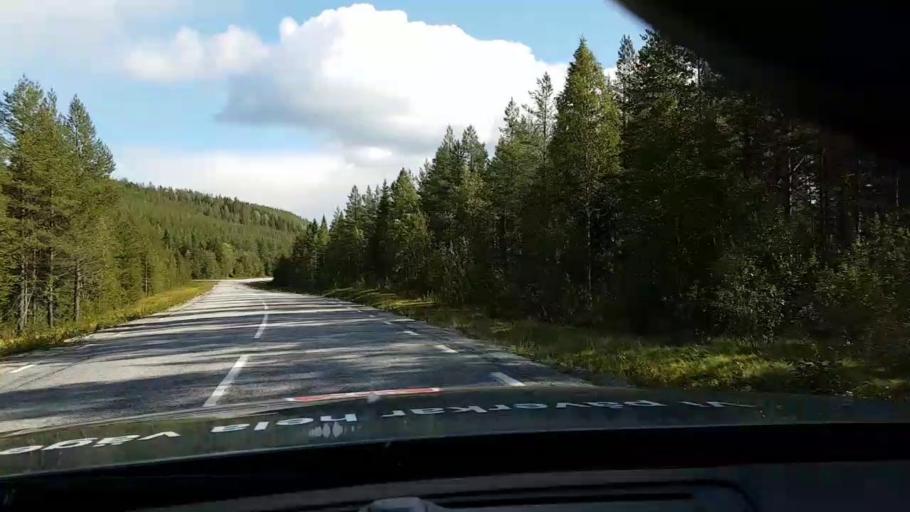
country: SE
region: Vaesternorrland
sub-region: OErnskoeldsviks Kommun
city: Bredbyn
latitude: 63.7593
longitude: 17.6958
